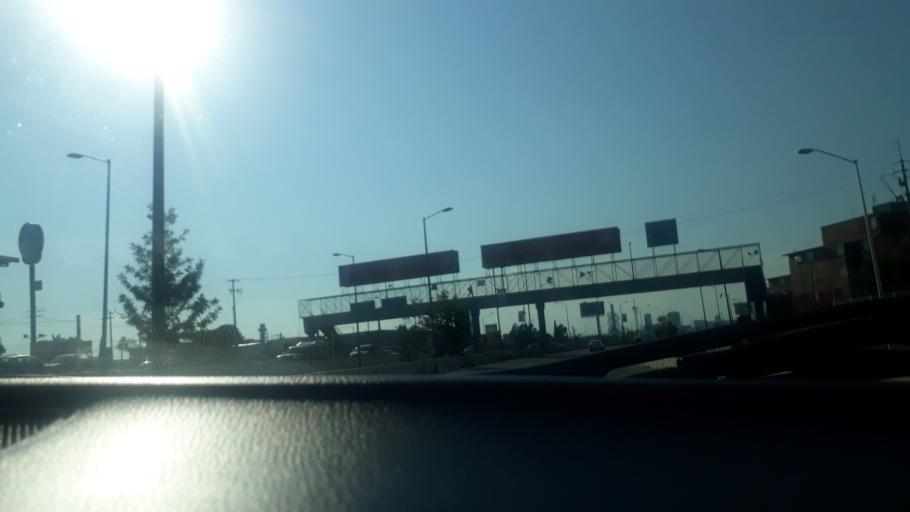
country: MX
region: Puebla
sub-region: Puebla
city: El Capulo (La Quebradora)
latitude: 18.9927
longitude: -98.2489
